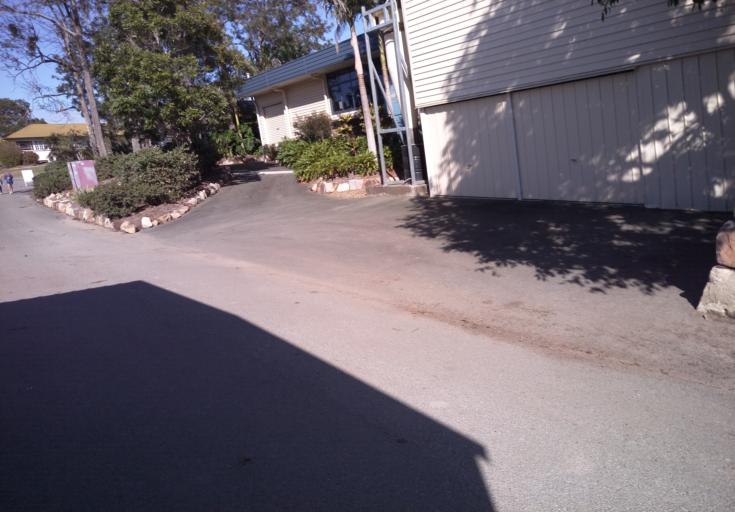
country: AU
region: Queensland
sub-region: Logan
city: Waterford West
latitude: -27.7069
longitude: 153.1494
